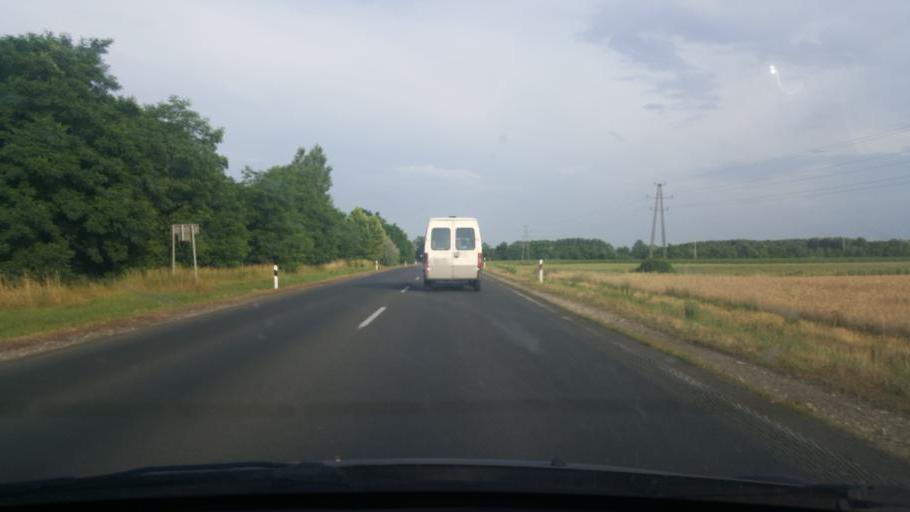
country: HU
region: Pest
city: Peteri
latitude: 47.3630
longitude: 19.3861
